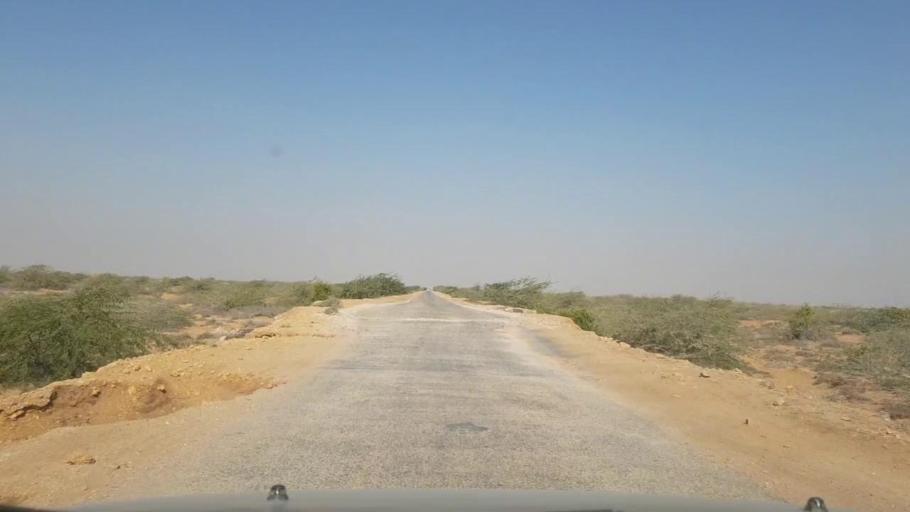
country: PK
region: Sindh
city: Thatta
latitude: 24.8273
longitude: 67.8927
